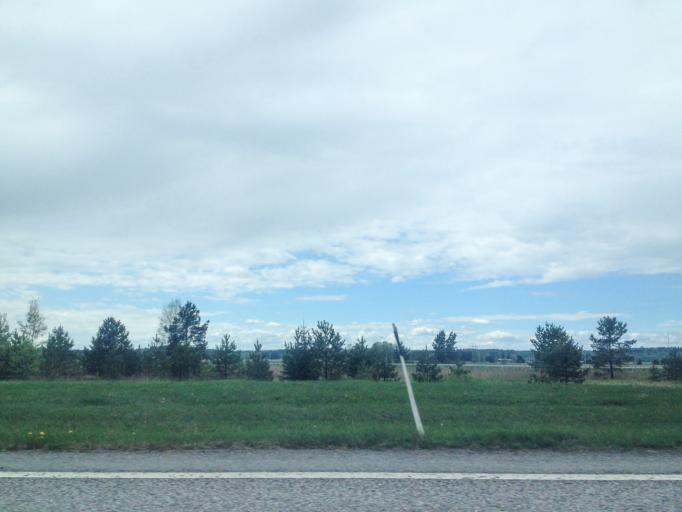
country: FI
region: Uusimaa
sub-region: Helsinki
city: Nurmijaervi
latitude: 60.5233
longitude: 24.8447
